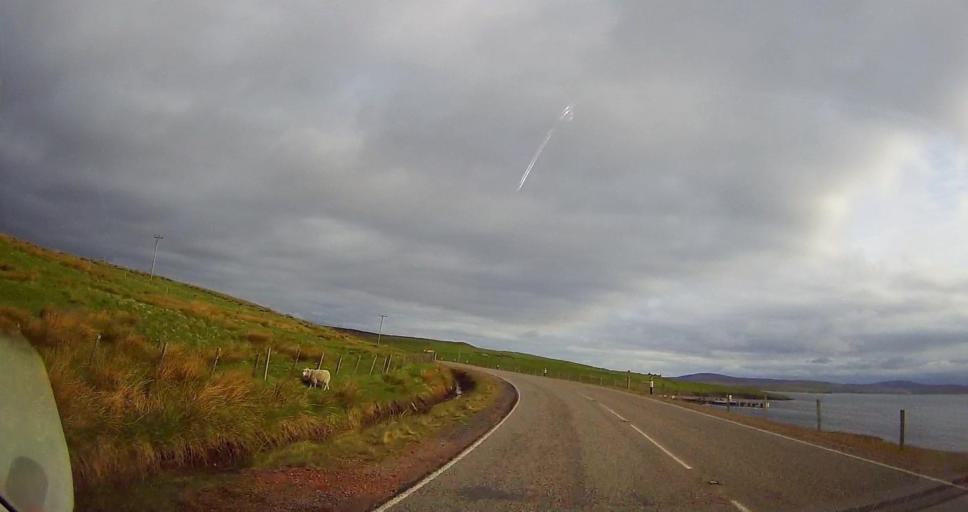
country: GB
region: Scotland
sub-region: Shetland Islands
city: Lerwick
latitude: 60.4604
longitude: -1.2096
